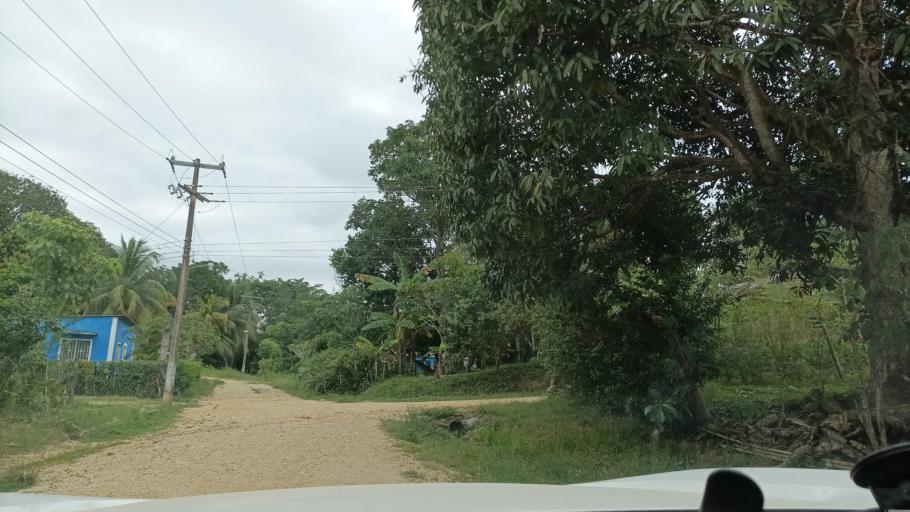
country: MX
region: Veracruz
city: Hidalgotitlan
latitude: 17.8073
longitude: -94.5380
